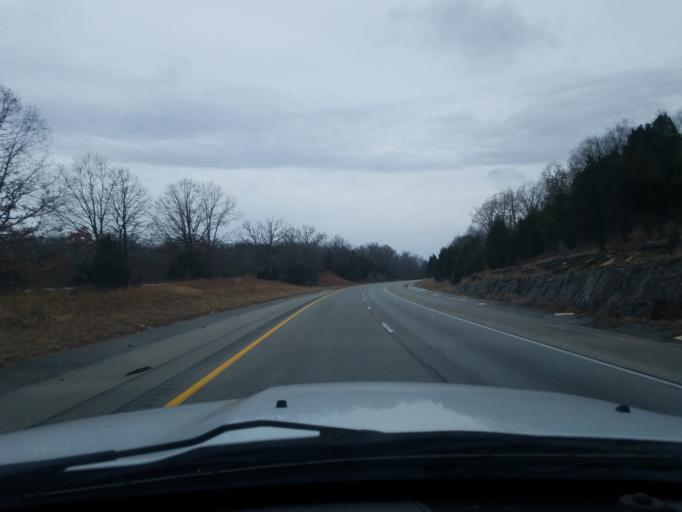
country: US
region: Indiana
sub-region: Harrison County
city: Corydon
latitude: 38.2411
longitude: -86.2573
